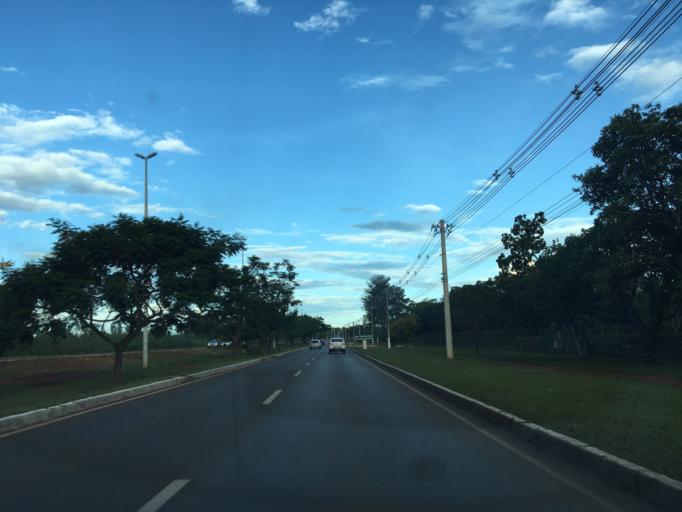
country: BR
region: Federal District
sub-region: Brasilia
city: Brasilia
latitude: -15.8152
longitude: -47.8551
